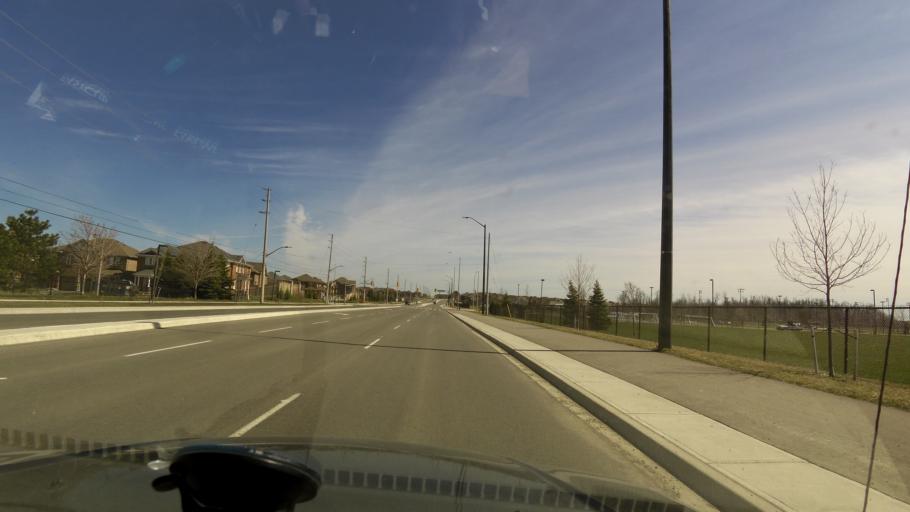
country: CA
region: Ontario
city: Brampton
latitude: 43.6868
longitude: -79.8329
